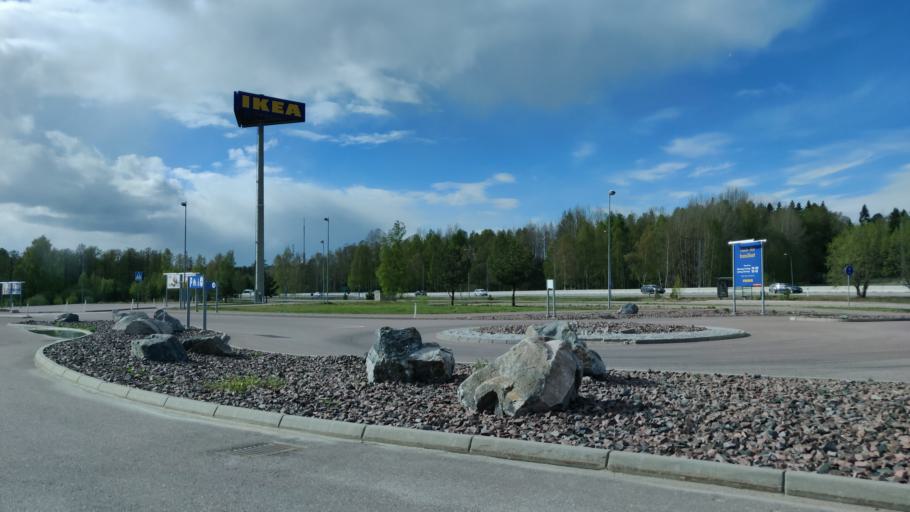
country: SE
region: Vaermland
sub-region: Hammaro Kommun
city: Skoghall
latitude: 59.3802
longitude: 13.4188
